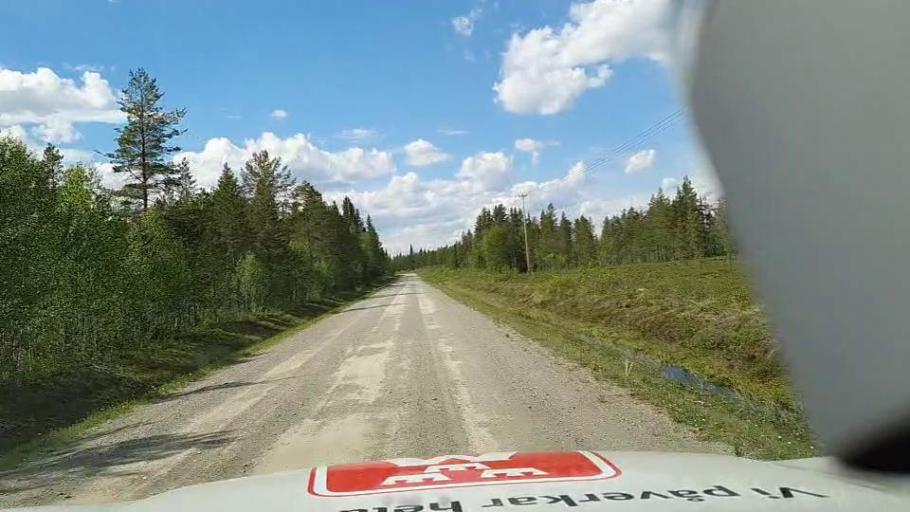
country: SE
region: Vaesterbotten
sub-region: Vilhelmina Kommun
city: Sjoberg
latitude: 64.5435
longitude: 15.6499
